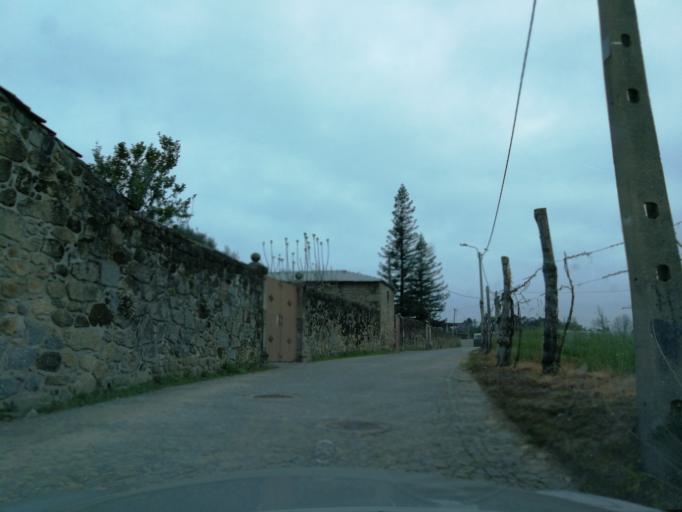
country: PT
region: Braga
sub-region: Braga
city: Braga
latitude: 41.5762
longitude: -8.4412
